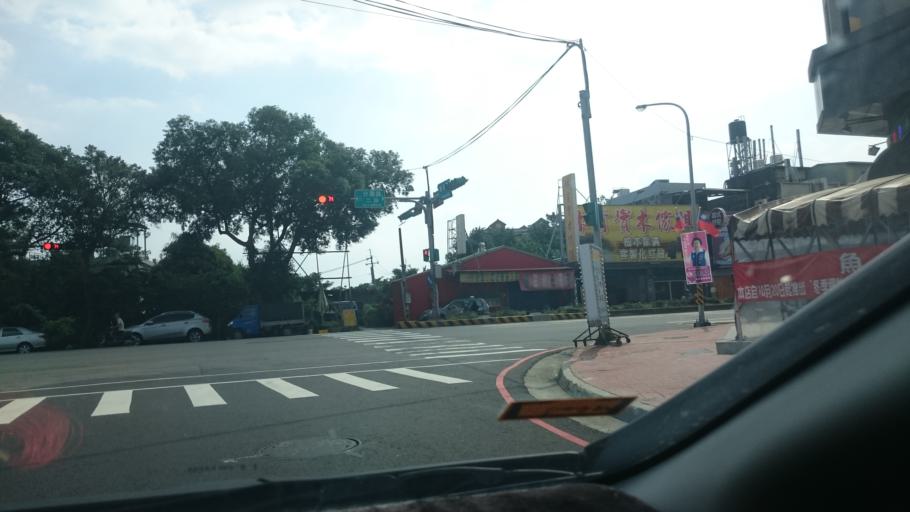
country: TW
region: Taiwan
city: Daxi
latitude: 24.9246
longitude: 121.2958
